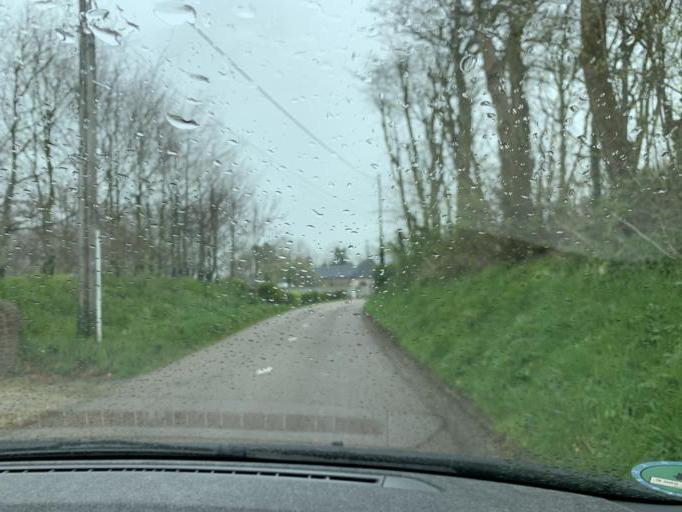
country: FR
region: Haute-Normandie
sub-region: Departement de la Seine-Maritime
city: Les Loges
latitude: 49.7185
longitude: 0.2701
